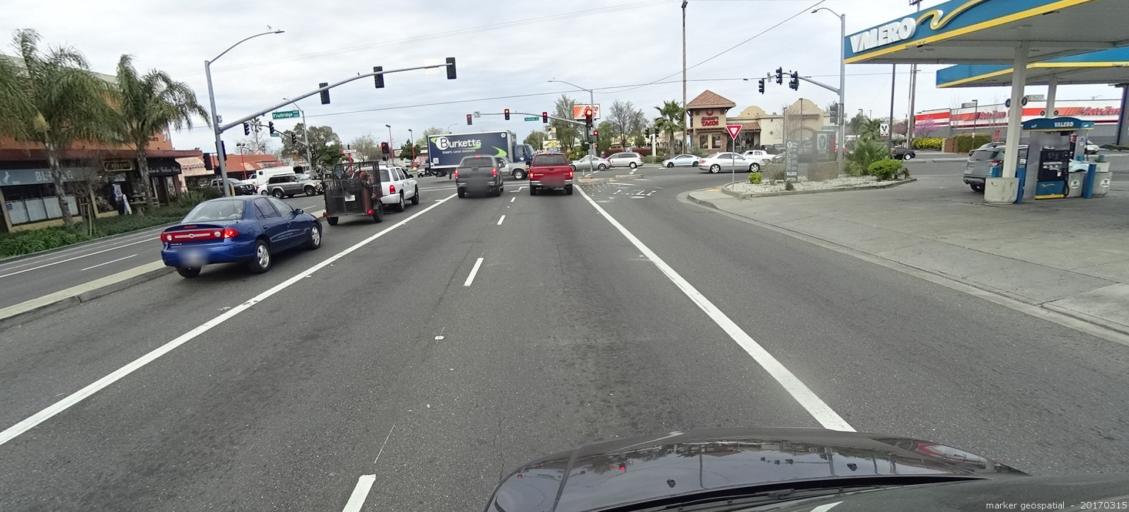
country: US
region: California
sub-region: Sacramento County
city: Parkway
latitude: 38.5245
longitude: -121.4716
